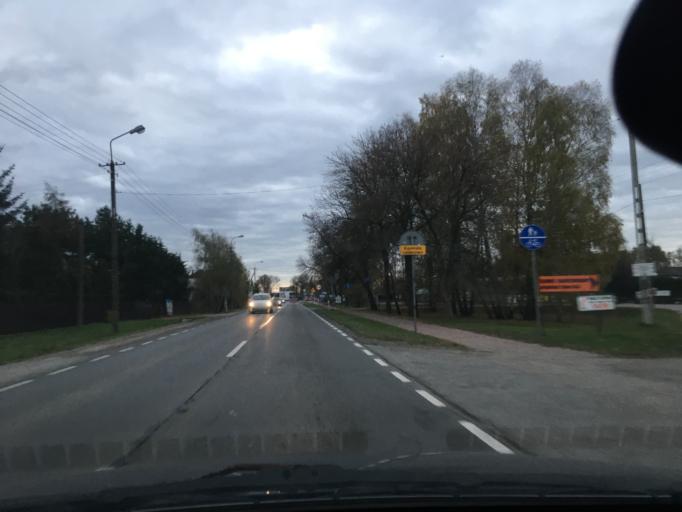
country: PL
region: Masovian Voivodeship
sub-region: Powiat piaseczynski
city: Lesznowola
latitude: 52.0921
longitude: 20.9316
